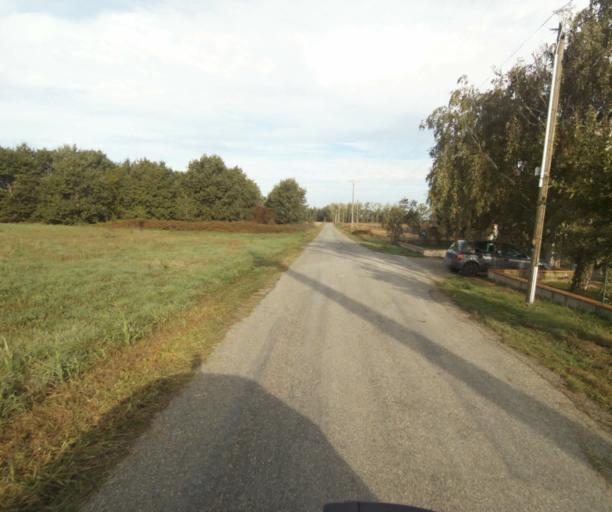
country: FR
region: Midi-Pyrenees
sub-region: Departement du Tarn-et-Garonne
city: Montech
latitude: 43.9735
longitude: 1.2286
